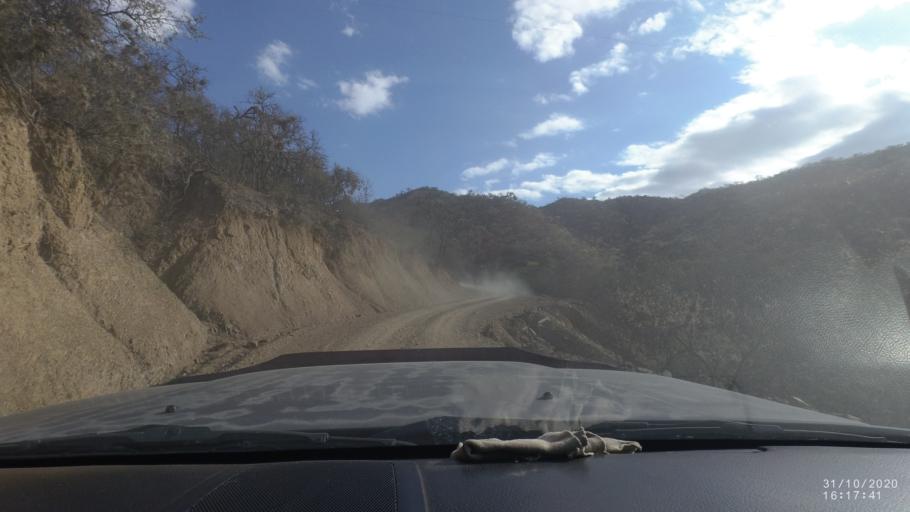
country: BO
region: Chuquisaca
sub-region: Provincia Zudanez
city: Mojocoya
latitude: -18.3918
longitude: -64.6046
